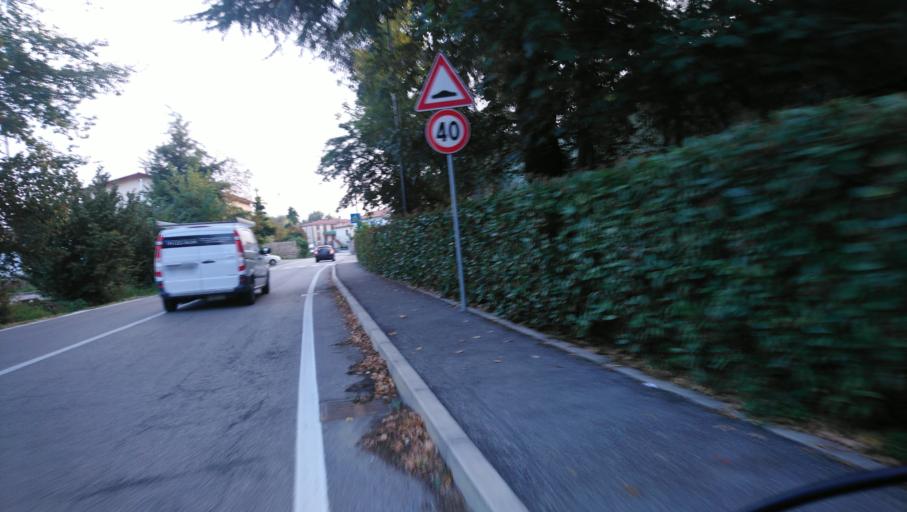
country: IT
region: Veneto
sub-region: Provincia di Treviso
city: Treviso
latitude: 45.6875
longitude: 12.2426
